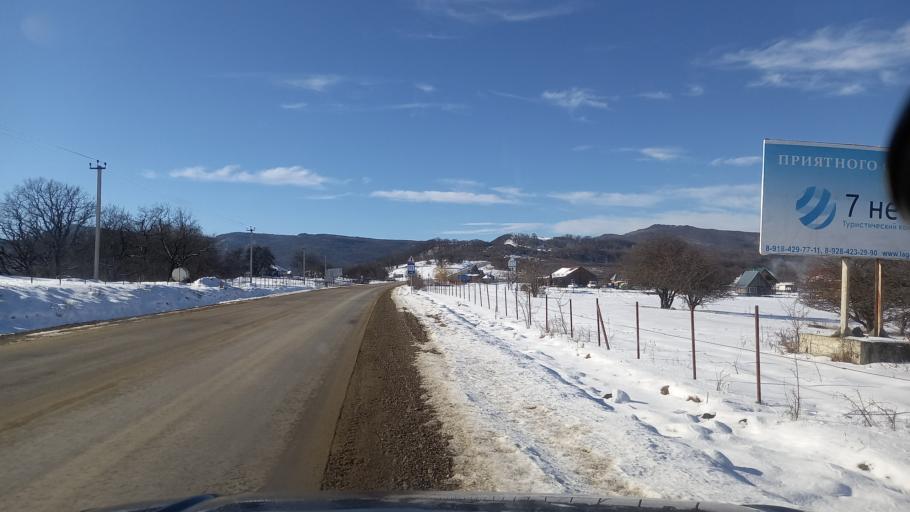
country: RU
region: Adygeya
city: Kamennomostskiy
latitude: 44.2349
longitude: 40.1505
